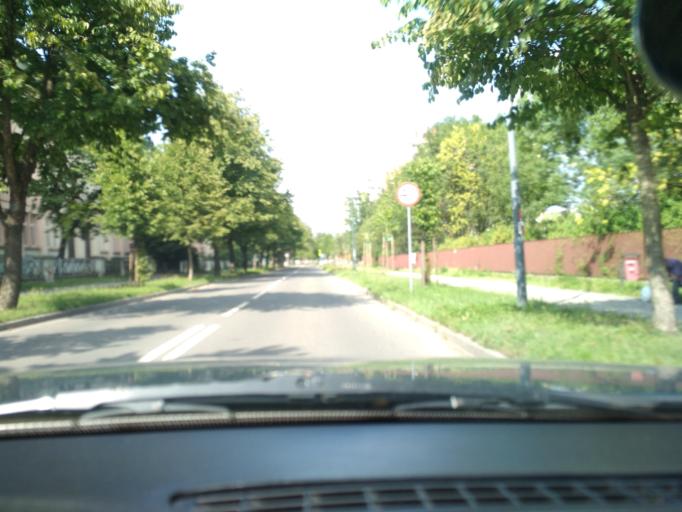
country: PL
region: Silesian Voivodeship
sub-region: Powiat raciborski
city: Raciborz
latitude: 50.0863
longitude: 18.2055
